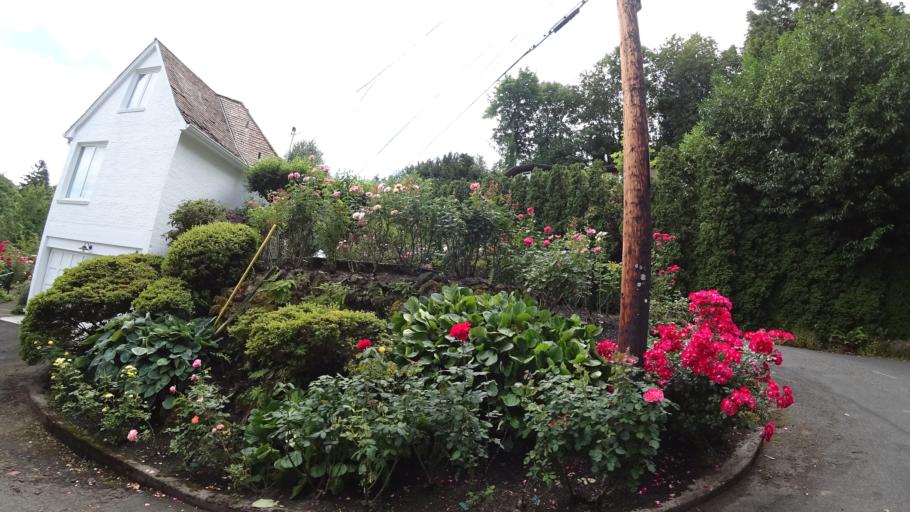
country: US
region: Oregon
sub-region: Multnomah County
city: Portland
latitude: 45.5277
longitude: -122.7108
